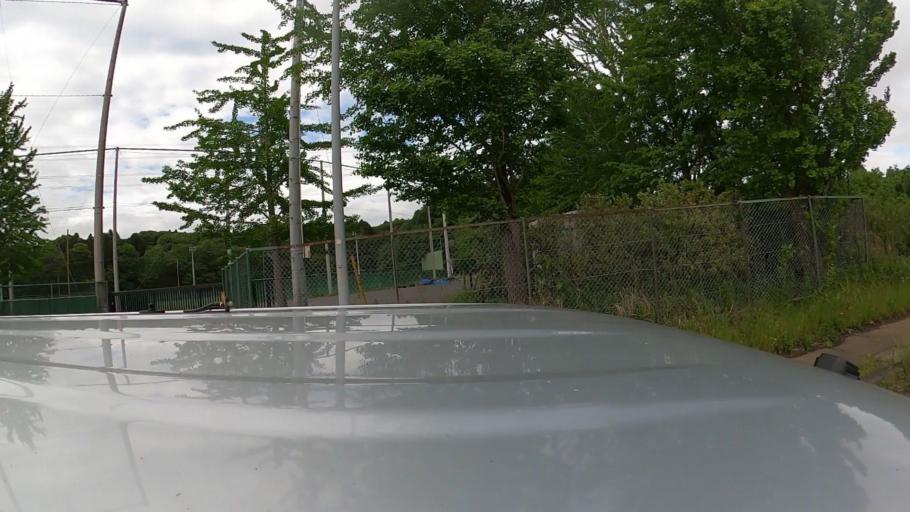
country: JP
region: Ibaraki
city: Ryugasaki
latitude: 35.9581
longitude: 140.2165
